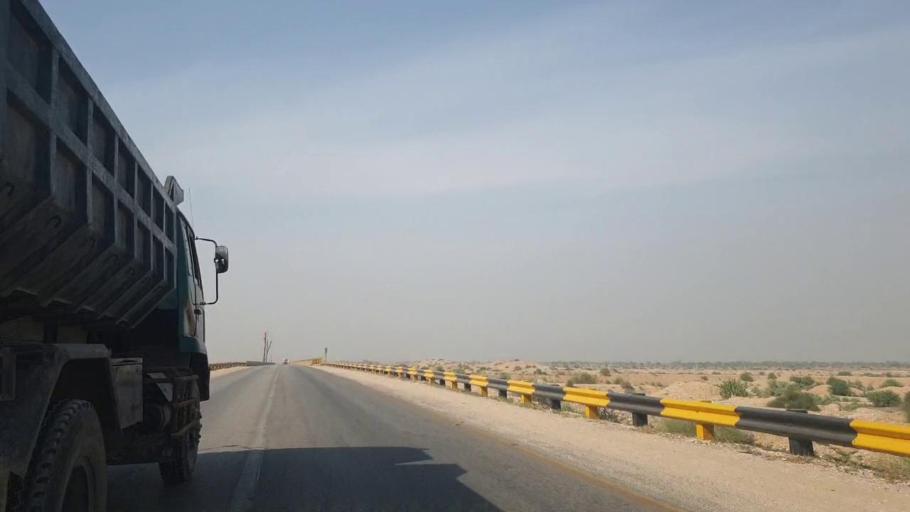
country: PK
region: Sindh
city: Sann
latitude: 26.0334
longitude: 68.1202
